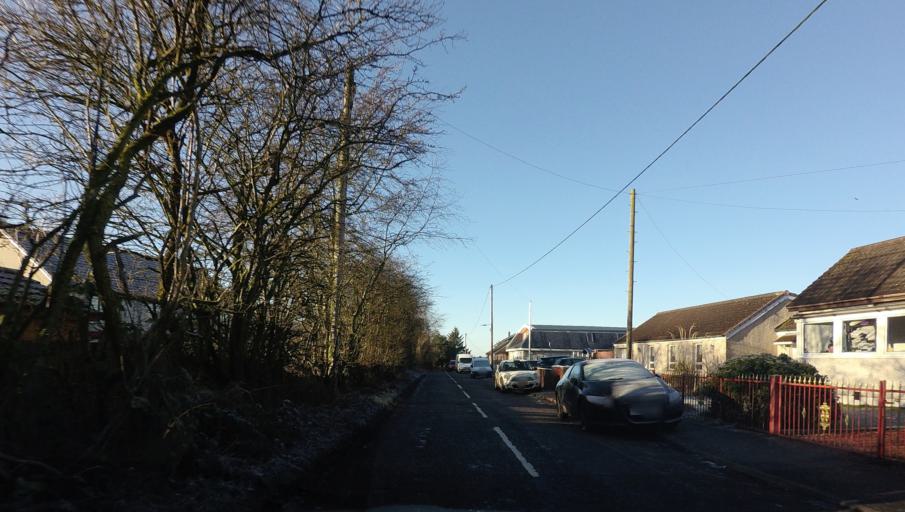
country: GB
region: Scotland
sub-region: North Lanarkshire
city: Cleland
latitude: 55.8029
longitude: -3.8921
